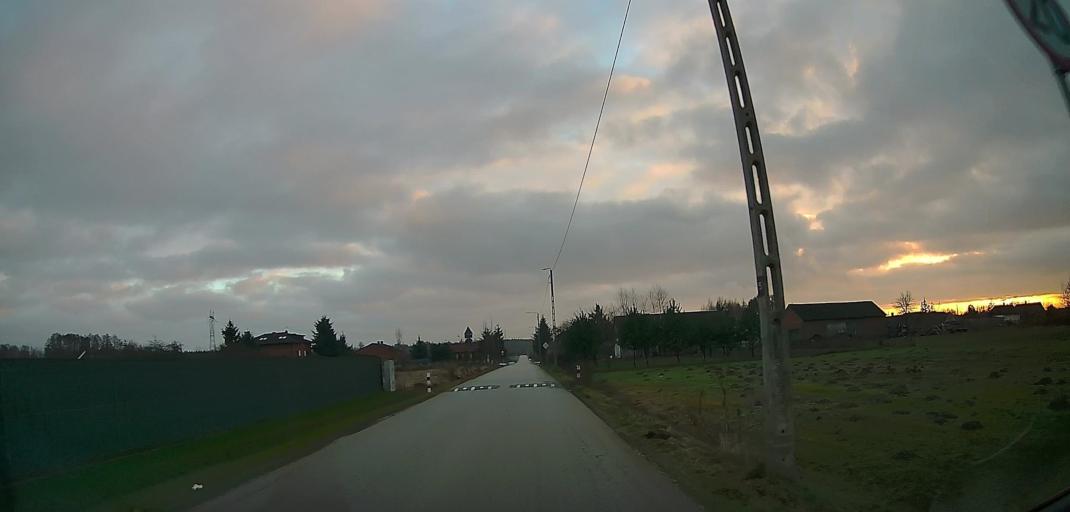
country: PL
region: Masovian Voivodeship
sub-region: Powiat radomski
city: Jedlinsk
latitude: 51.4585
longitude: 21.1236
